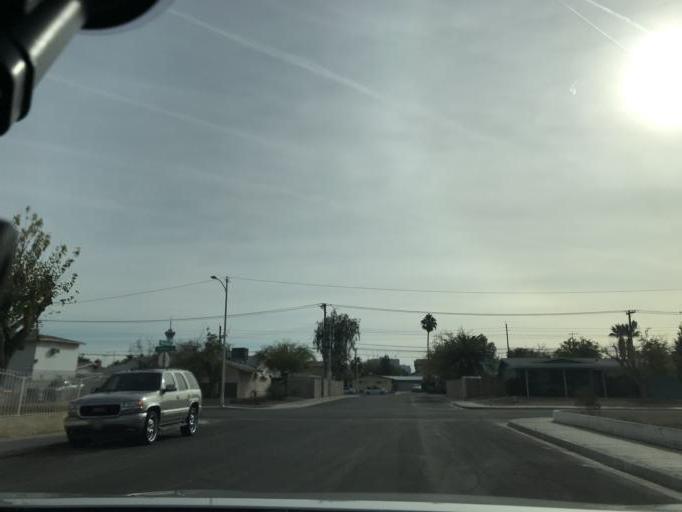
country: US
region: Nevada
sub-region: Clark County
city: Las Vegas
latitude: 36.1712
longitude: -115.1682
